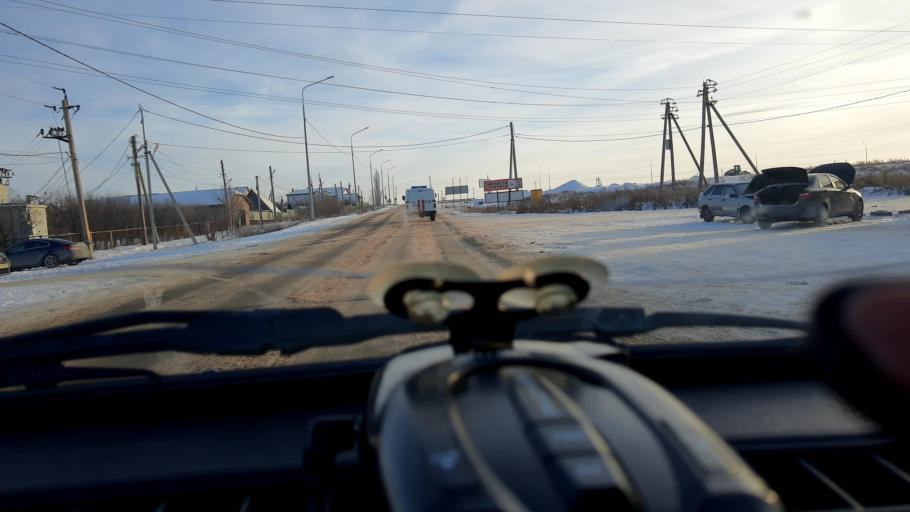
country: RU
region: Bashkortostan
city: Avdon
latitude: 54.6066
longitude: 55.8453
